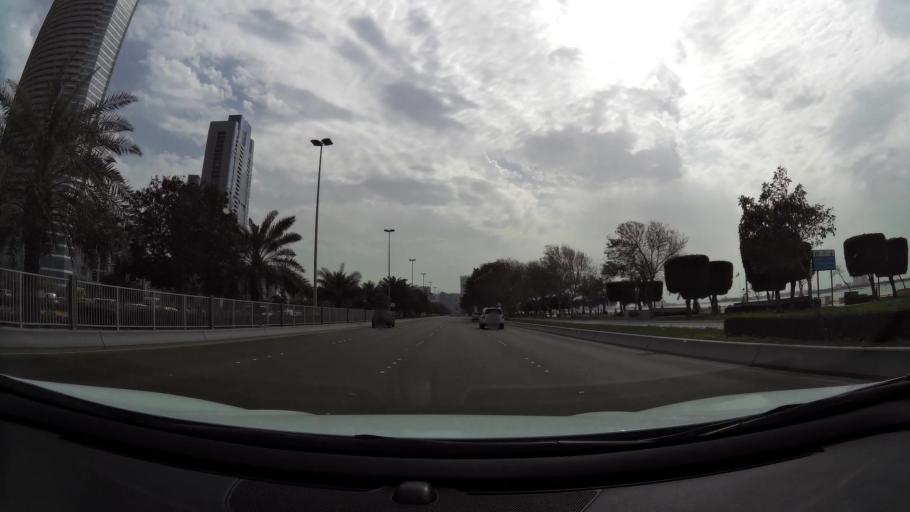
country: AE
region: Abu Dhabi
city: Abu Dhabi
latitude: 24.4865
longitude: 54.3494
